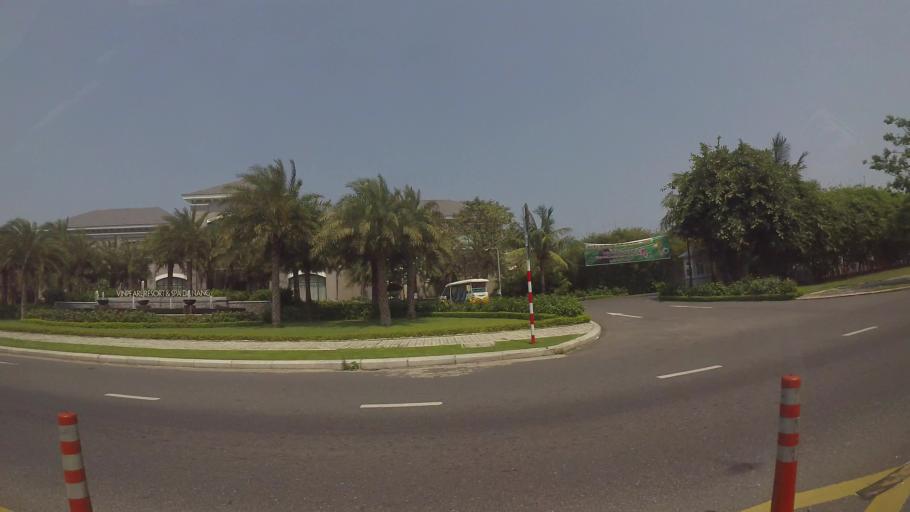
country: VN
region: Da Nang
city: Ngu Hanh Son
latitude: 15.9938
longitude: 108.2687
